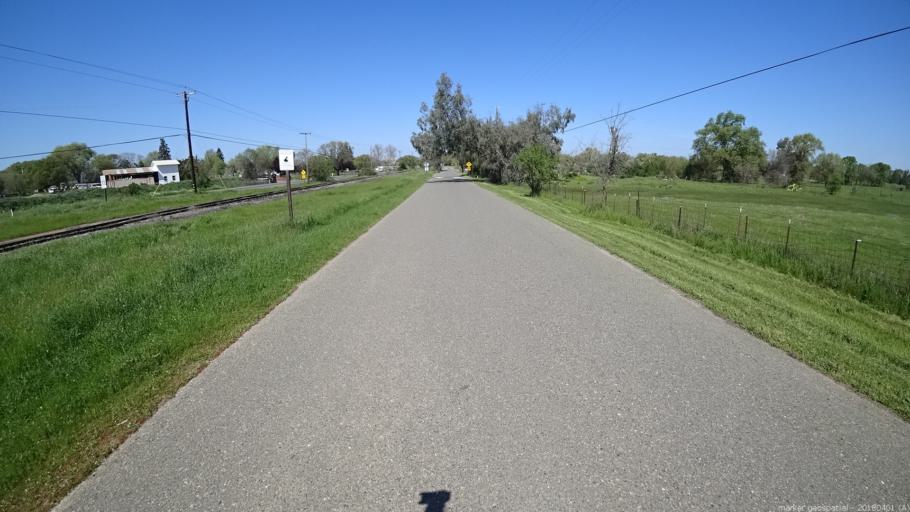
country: US
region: California
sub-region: Sacramento County
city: Wilton
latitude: 38.4124
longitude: -121.2725
